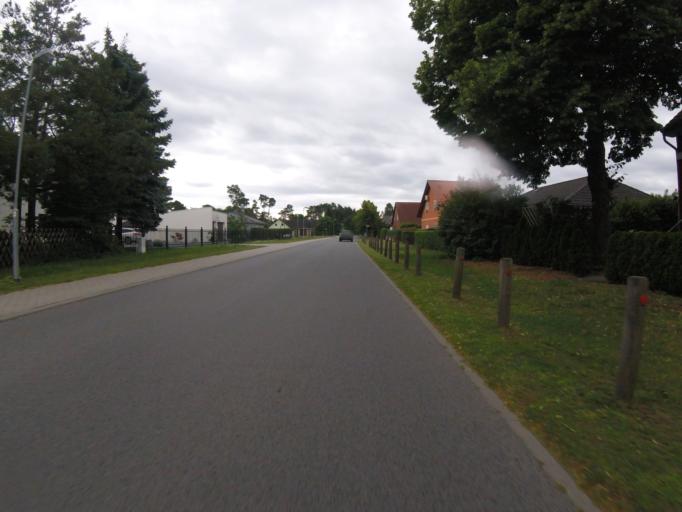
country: DE
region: Brandenburg
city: Bestensee
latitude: 52.2296
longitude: 13.6380
